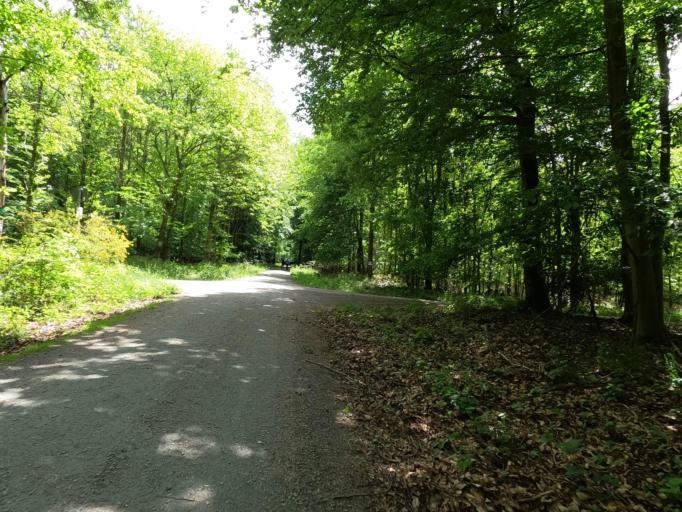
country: DE
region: Hesse
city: Langen
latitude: 50.0060
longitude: 8.6361
